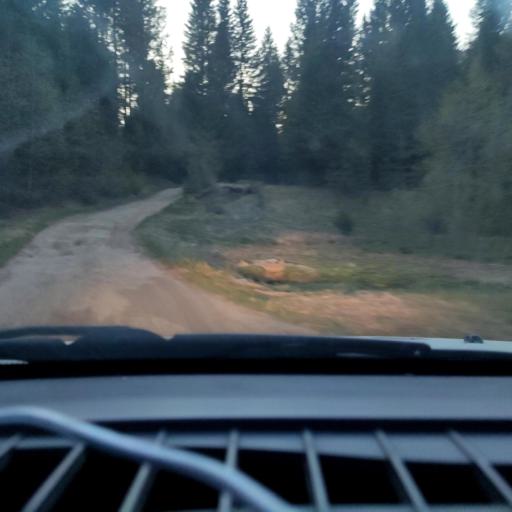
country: RU
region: Perm
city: Perm
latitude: 58.1542
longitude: 56.2913
